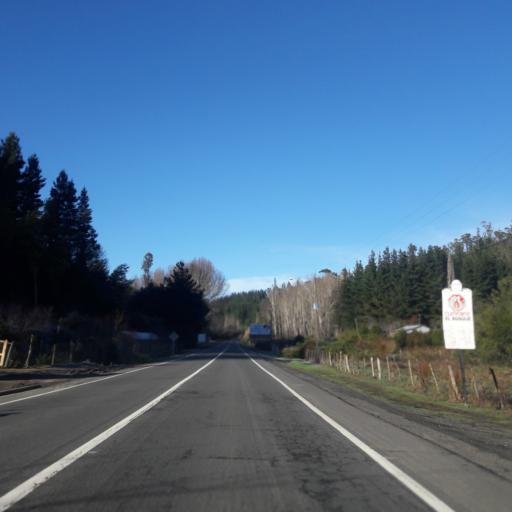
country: CL
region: Biobio
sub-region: Provincia de Concepcion
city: Lota
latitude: -37.2386
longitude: -72.9642
